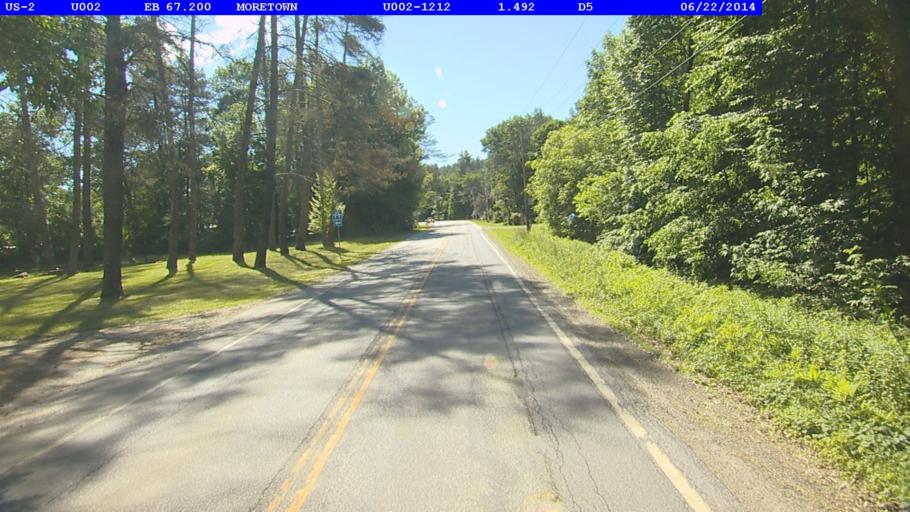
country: US
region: Vermont
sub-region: Washington County
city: Waterbury
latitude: 44.3135
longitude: -72.7241
